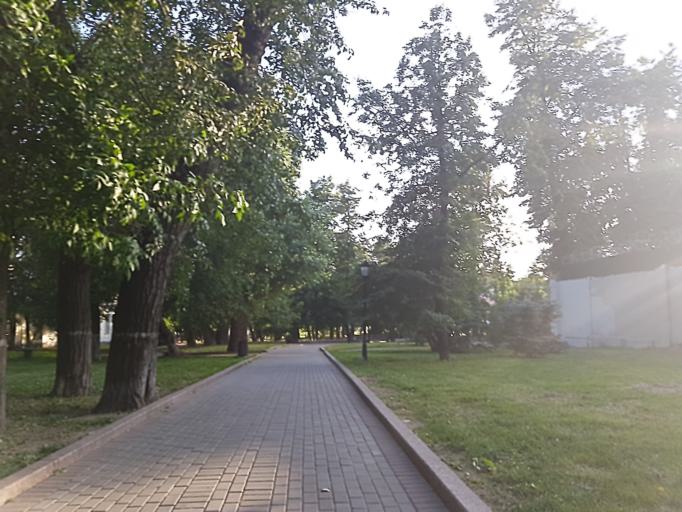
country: RU
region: Moscow
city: Sokol'niki
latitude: 55.7734
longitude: 37.6710
